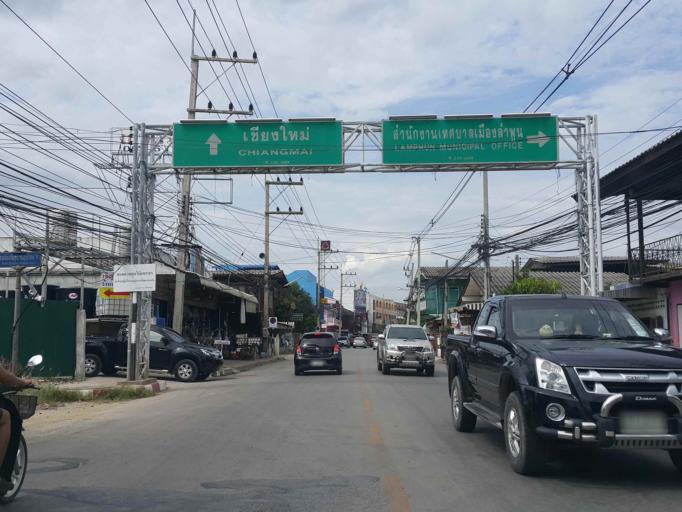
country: TH
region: Lamphun
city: Lamphun
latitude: 18.5866
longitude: 99.0100
